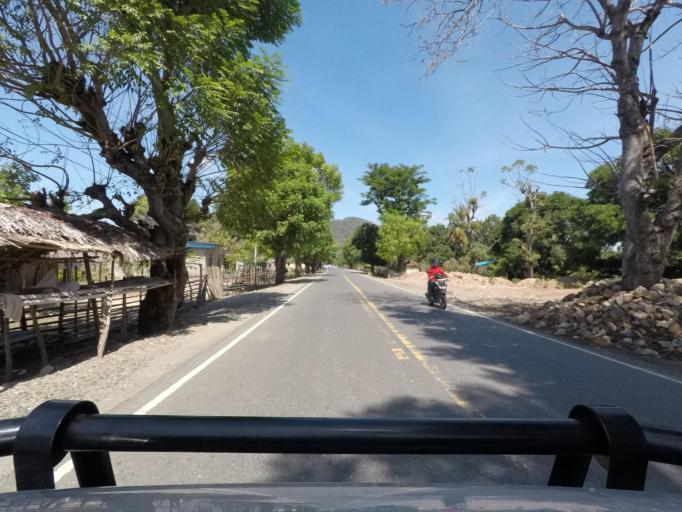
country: TL
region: Liquica
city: Maubara
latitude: -8.7901
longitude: 125.1015
